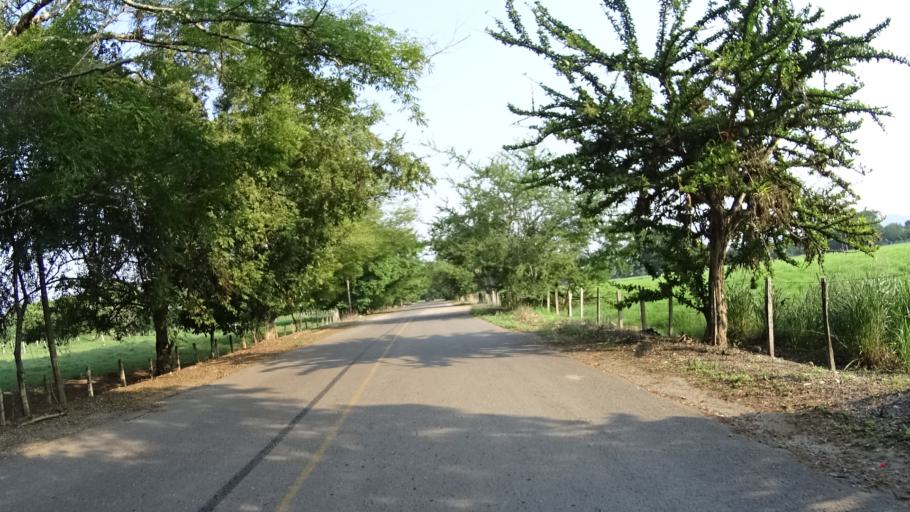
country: CO
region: Cundinamarca
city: Puerto Salgar
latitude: 5.4970
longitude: -74.6847
